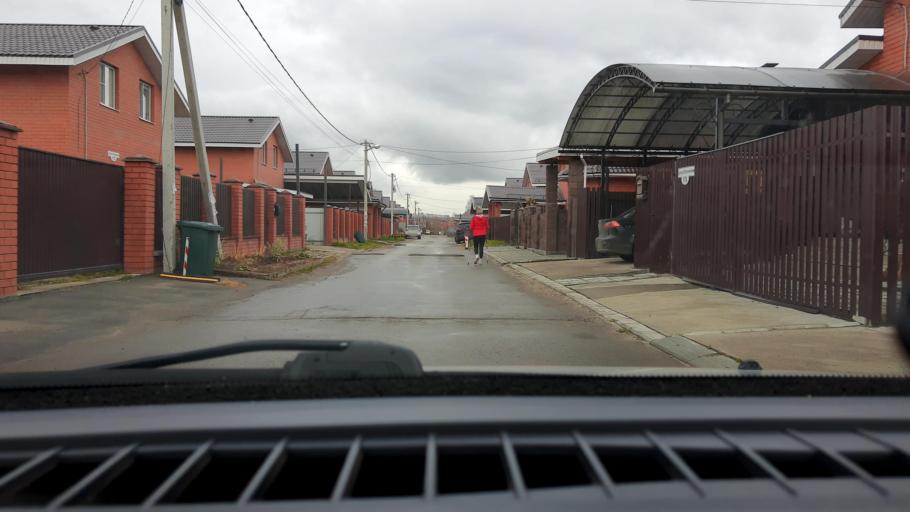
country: RU
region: Nizjnij Novgorod
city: Afonino
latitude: 56.2026
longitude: 44.1270
